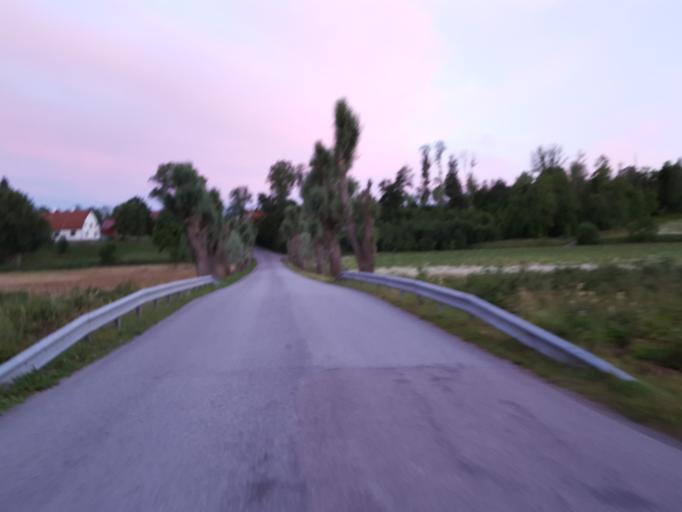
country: SE
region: Uppsala
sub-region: Uppsala Kommun
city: Uppsala
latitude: 59.7857
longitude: 17.5979
